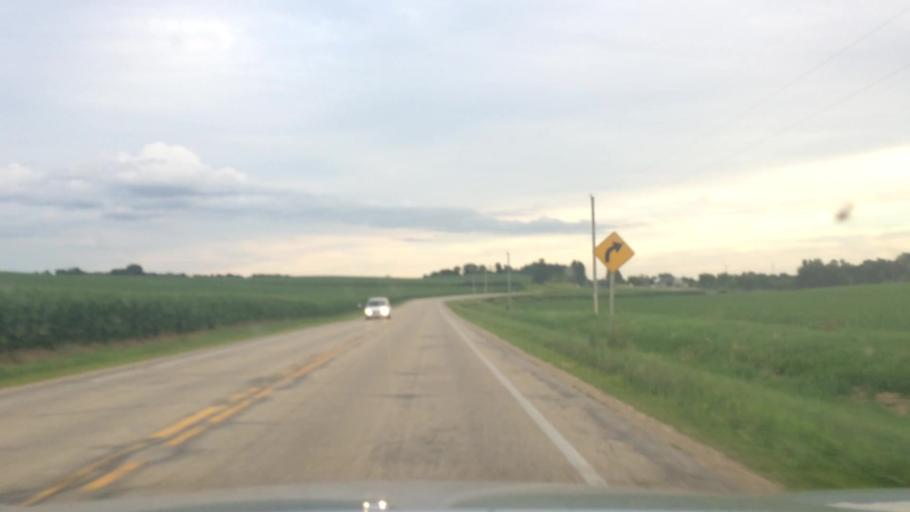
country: US
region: Wisconsin
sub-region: Dane County
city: Waunakee
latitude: 43.2149
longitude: -89.5461
